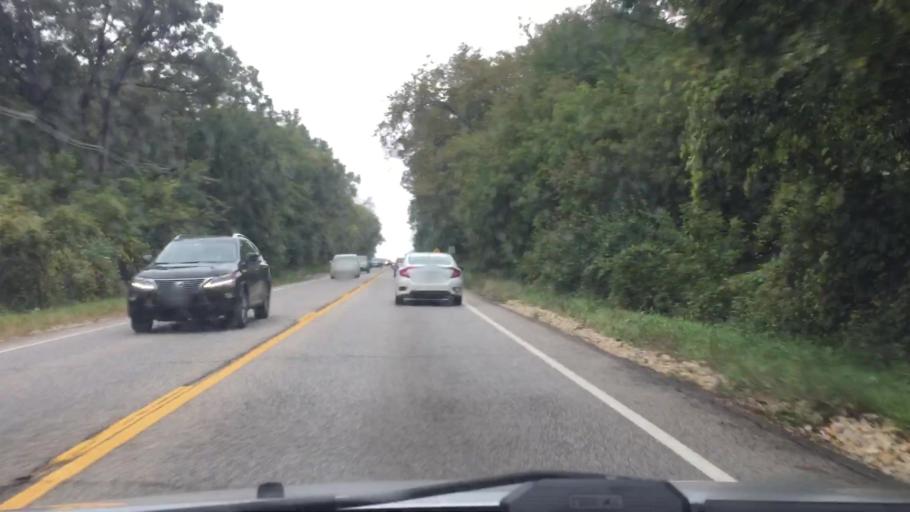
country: US
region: Illinois
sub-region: McHenry County
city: Prairie Grove
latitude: 42.2631
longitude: -88.2868
